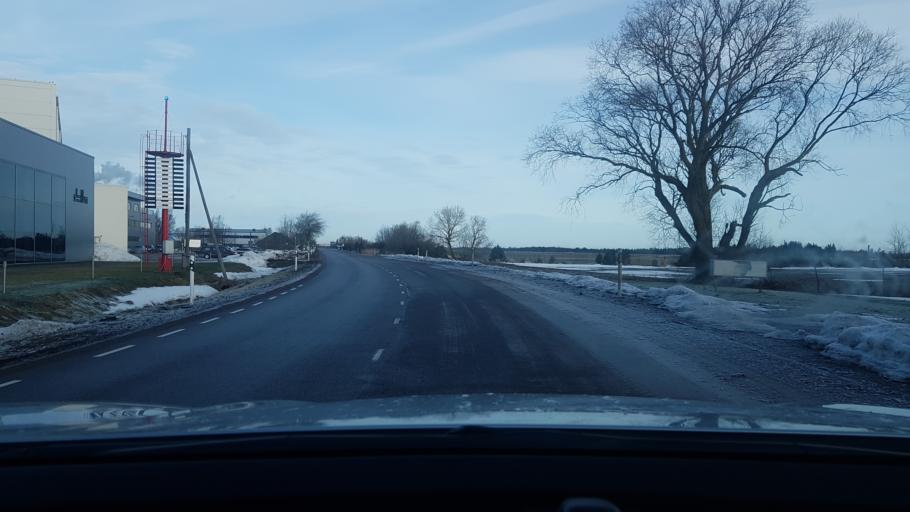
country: EE
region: Saare
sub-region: Kuressaare linn
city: Kuressaare
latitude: 58.2201
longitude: 22.5071
